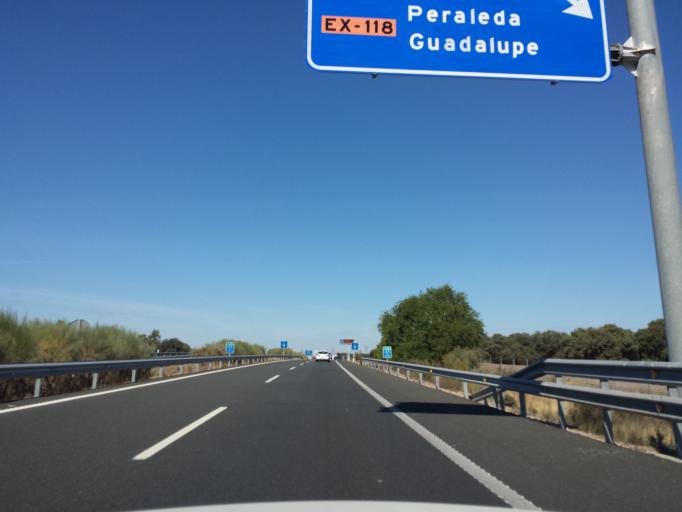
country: ES
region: Extremadura
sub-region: Provincia de Caceres
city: Navalmoral de la Mata
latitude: 39.8892
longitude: -5.5002
